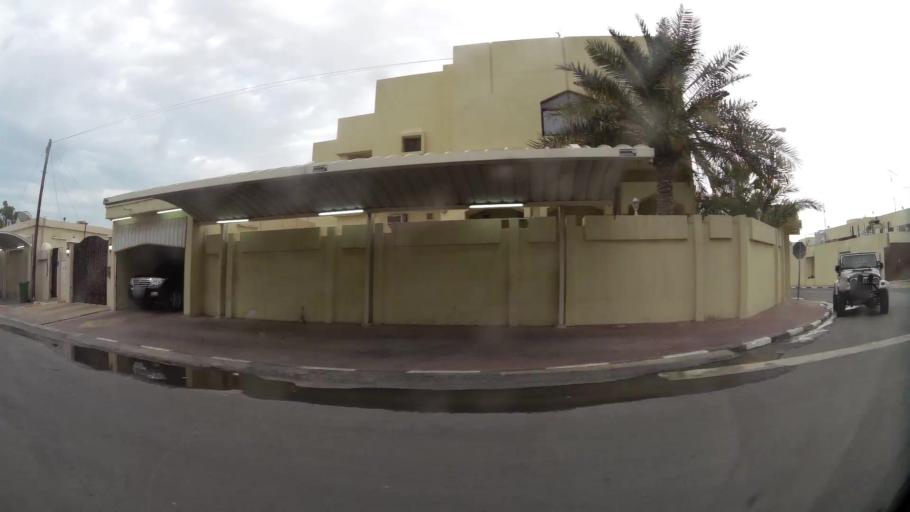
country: QA
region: Baladiyat ad Dawhah
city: Doha
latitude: 25.2718
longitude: 51.4983
